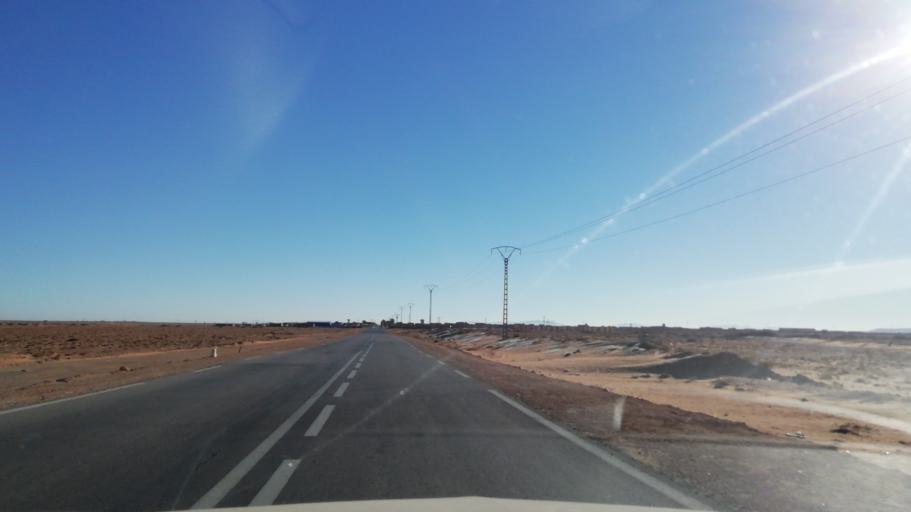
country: DZ
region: El Bayadh
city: El Bayadh
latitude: 33.8535
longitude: 0.6161
